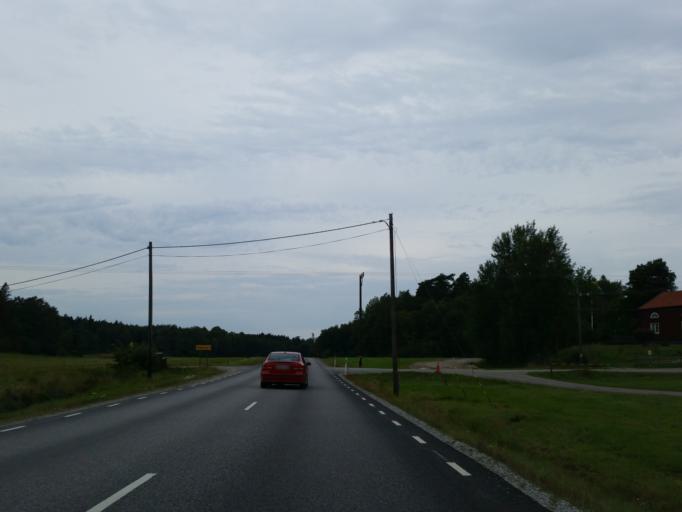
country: SE
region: Stockholm
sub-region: Salems Kommun
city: Ronninge
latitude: 59.2206
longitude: 17.7520
